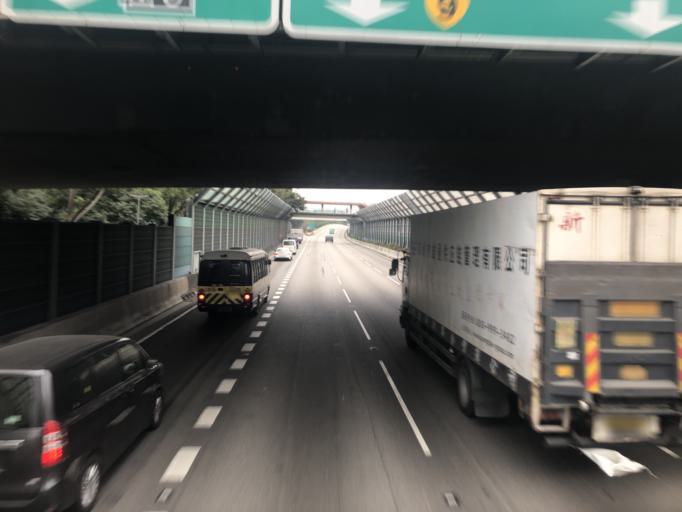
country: HK
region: Tai Po
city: Tai Po
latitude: 22.4989
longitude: 114.1275
